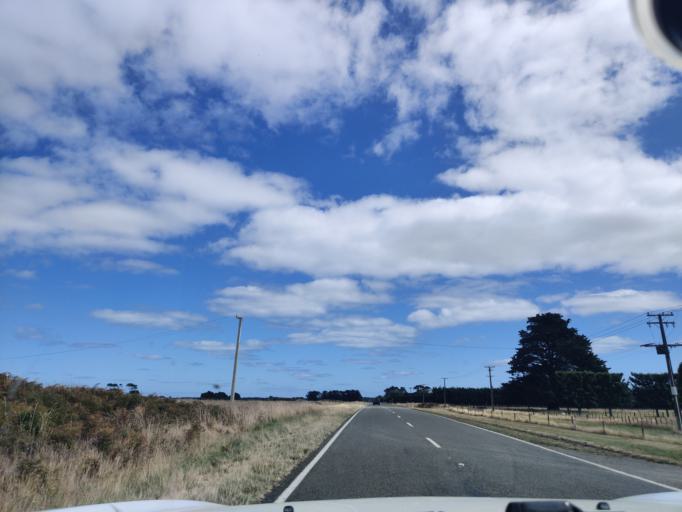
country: NZ
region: Manawatu-Wanganui
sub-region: Horowhenua District
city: Foxton
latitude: -40.3947
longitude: 175.3319
